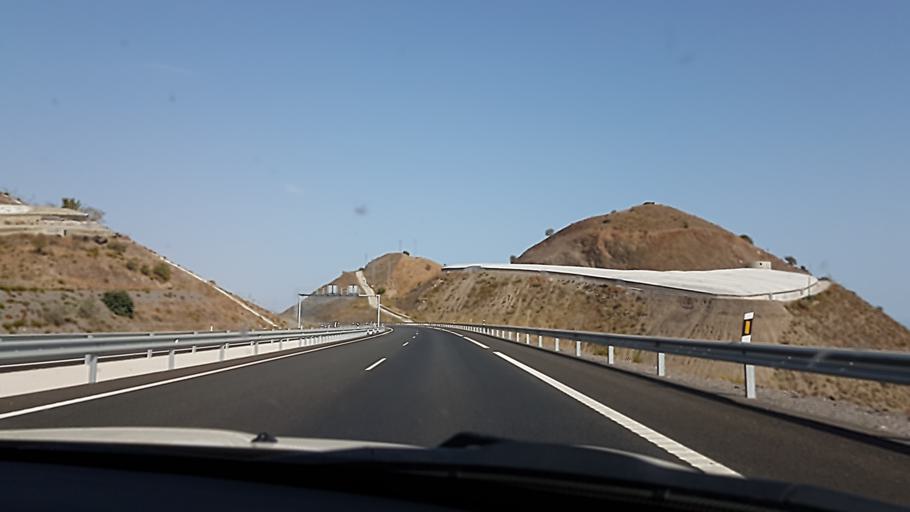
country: ES
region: Andalusia
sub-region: Provincia de Granada
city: Polopos
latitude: 36.7515
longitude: -3.2875
